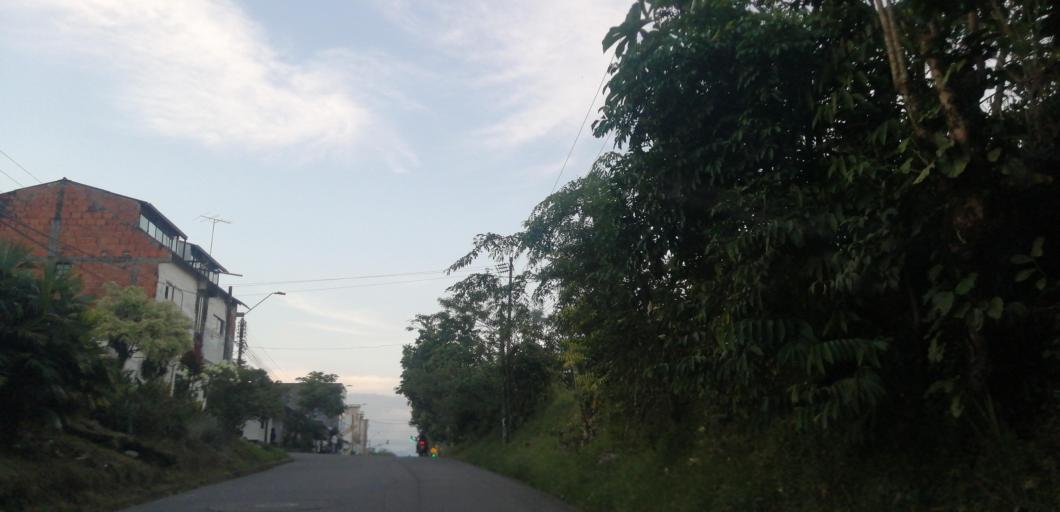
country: CO
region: Meta
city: Acacias
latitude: 3.9891
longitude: -73.7573
